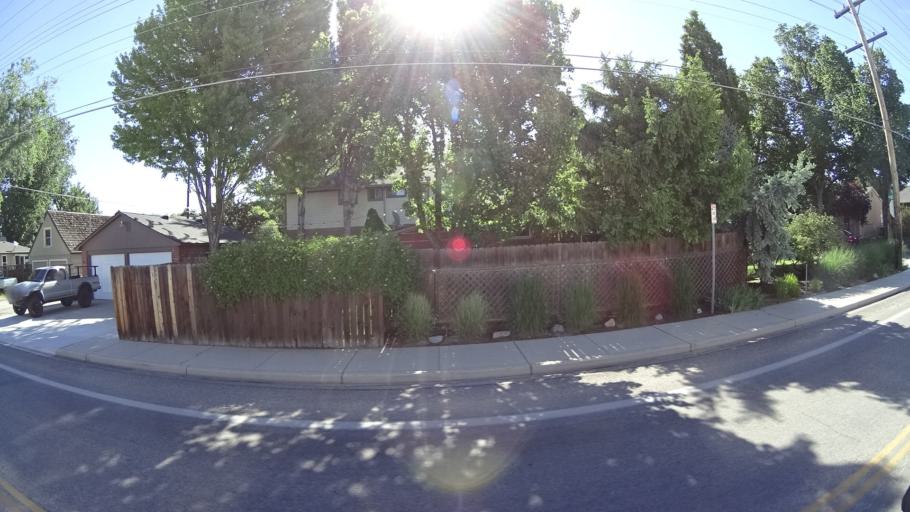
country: US
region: Idaho
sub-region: Ada County
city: Garden City
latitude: 43.6284
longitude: -116.2240
